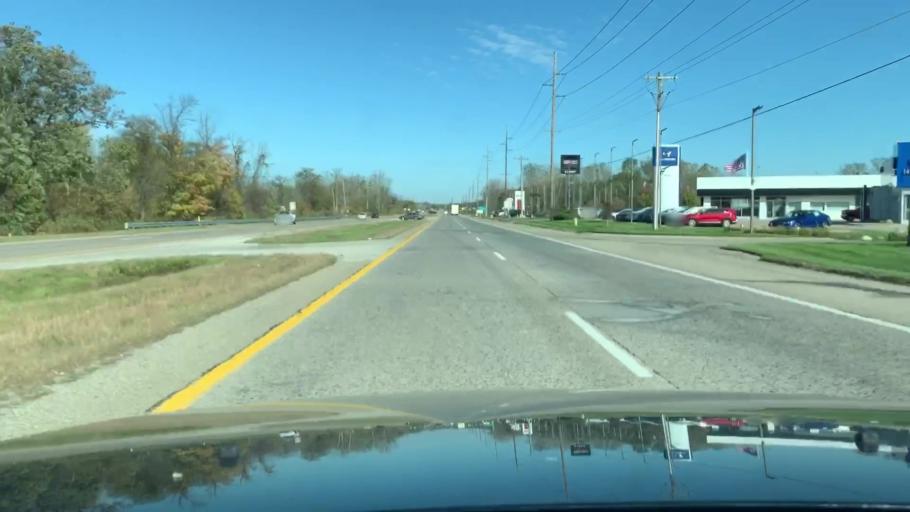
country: US
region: Michigan
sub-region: Ottawa County
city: Holland
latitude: 42.7992
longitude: -86.0736
